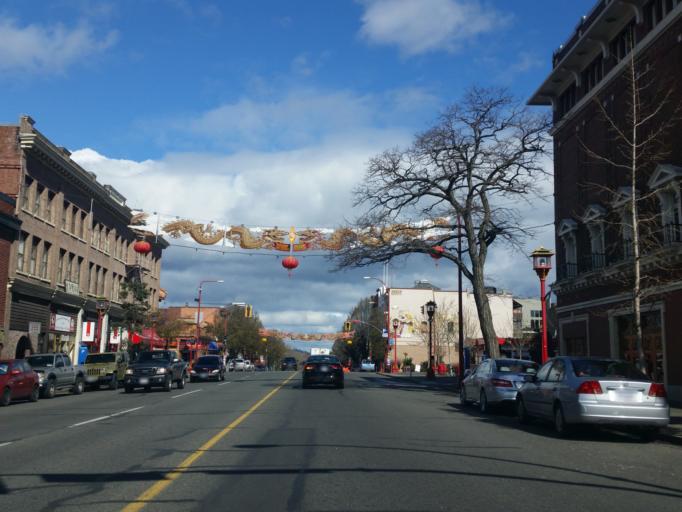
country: CA
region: British Columbia
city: Victoria
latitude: 48.4287
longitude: -123.3670
